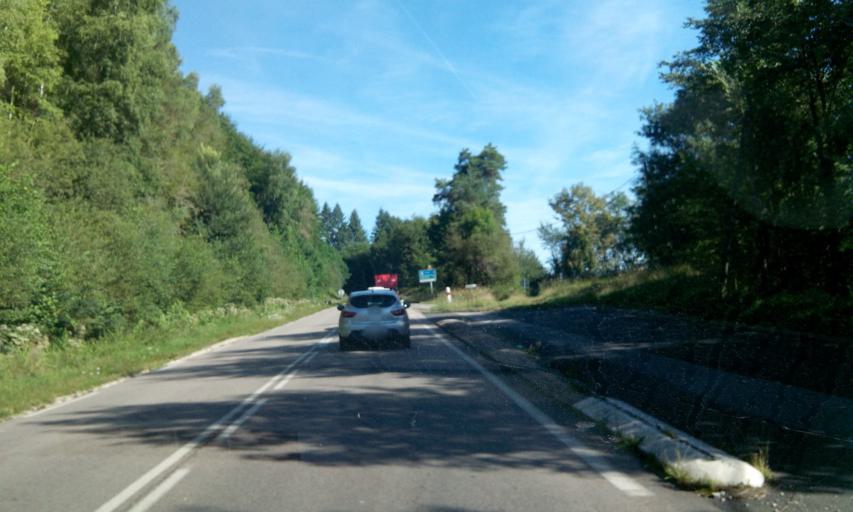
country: FR
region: Limousin
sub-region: Departement de la Haute-Vienne
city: Saint-Leonard-de-Noblat
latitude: 45.8384
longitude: 1.4677
